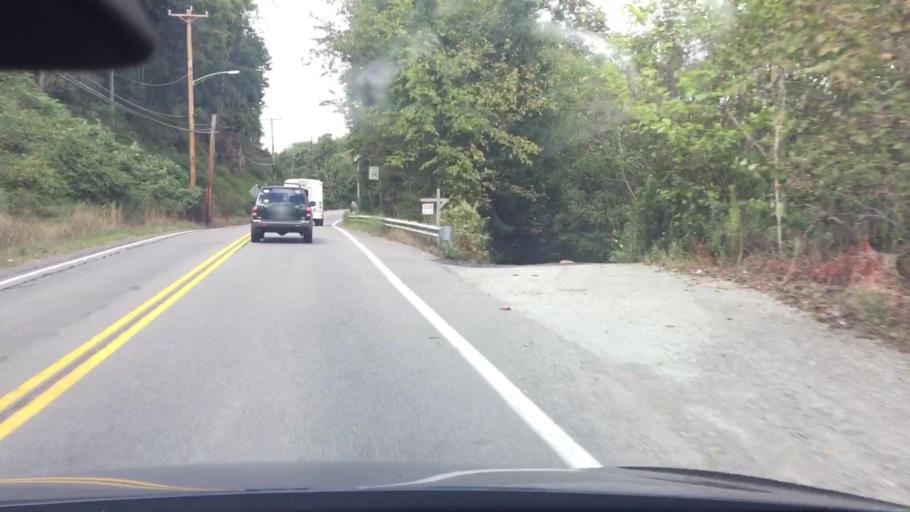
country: US
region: Pennsylvania
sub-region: Allegheny County
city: Cheswick
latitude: 40.5111
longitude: -79.8003
